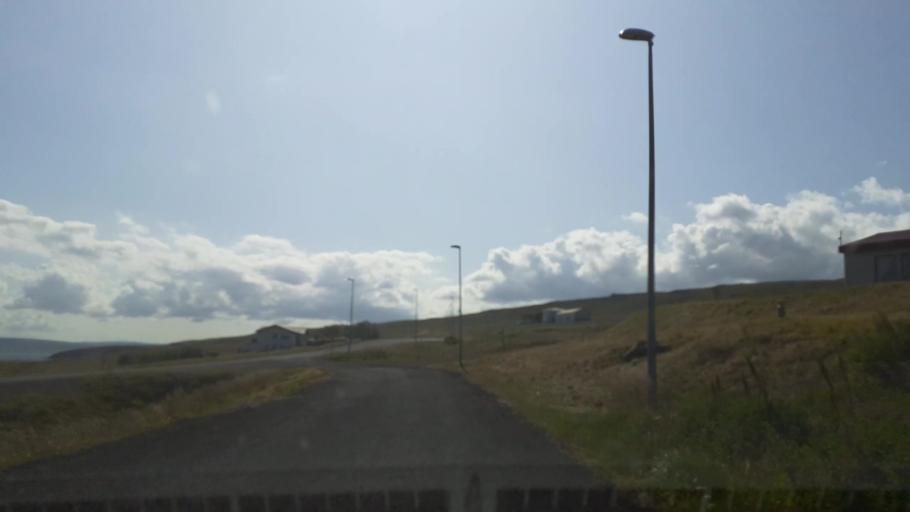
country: IS
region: West
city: Borgarnes
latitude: 65.2072
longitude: -21.0987
